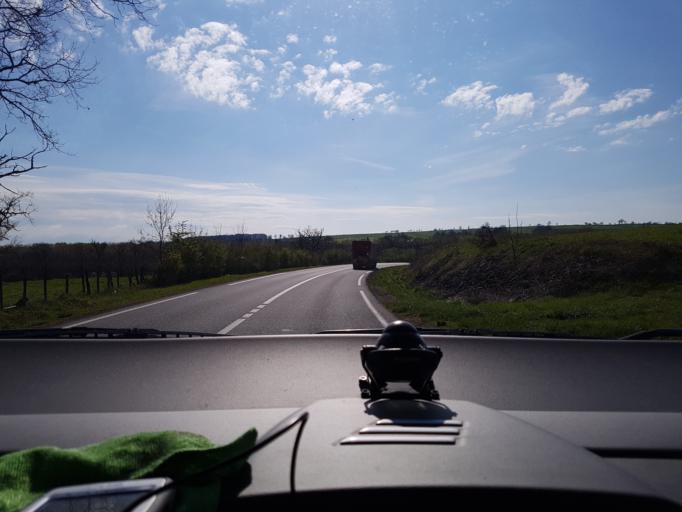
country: FR
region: Midi-Pyrenees
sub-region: Departement de l'Aveyron
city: Moyrazes
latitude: 44.3791
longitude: 2.4564
